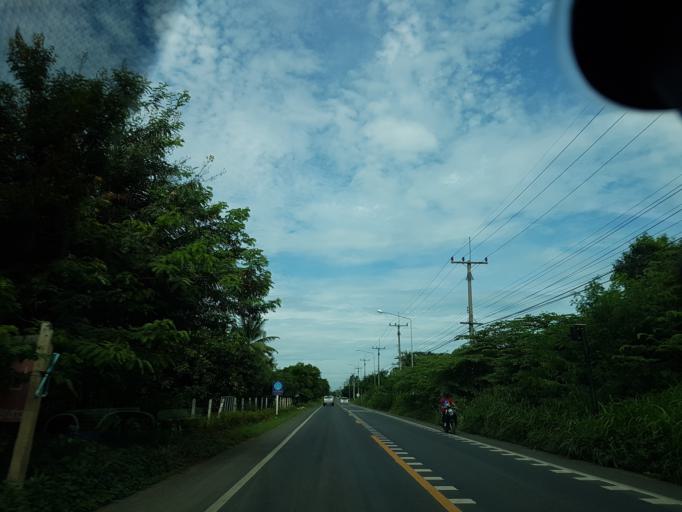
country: TH
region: Lop Buri
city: Tha Wung
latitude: 14.7398
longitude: 100.5304
